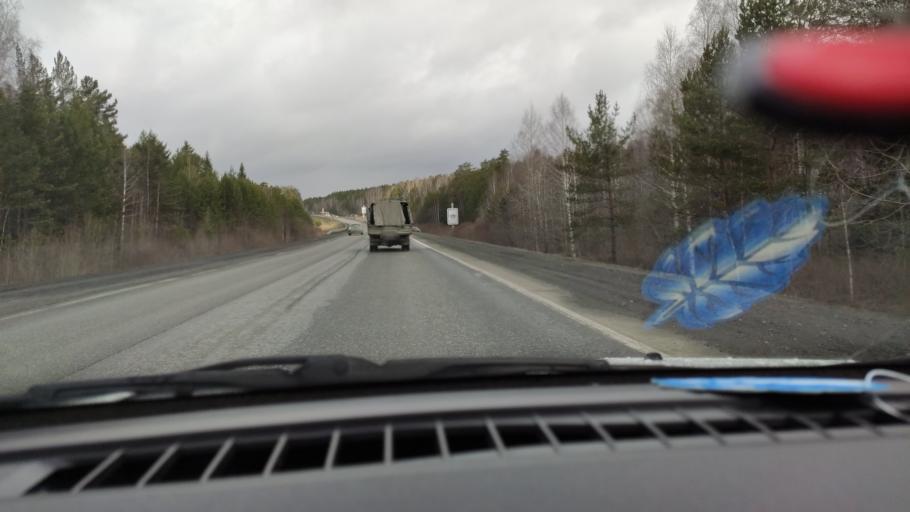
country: RU
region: Sverdlovsk
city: Talitsa
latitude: 56.8667
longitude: 60.0459
